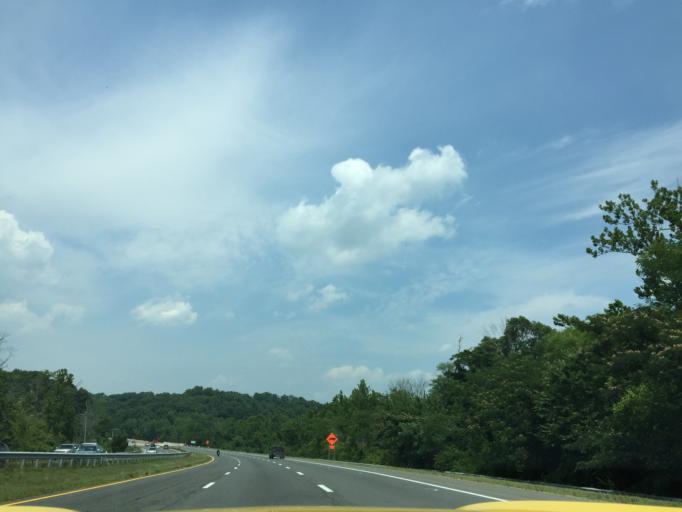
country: US
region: Maryland
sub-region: Prince George's County
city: Fort Washington
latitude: 38.6948
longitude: -76.9872
